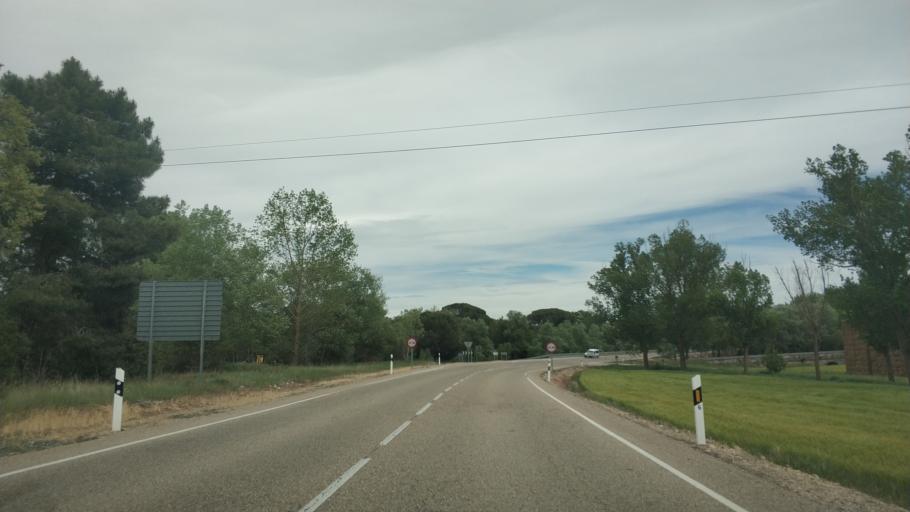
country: ES
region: Castille and Leon
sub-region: Provincia de Soria
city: Bayubas de Abajo
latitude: 41.5044
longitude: -2.8911
